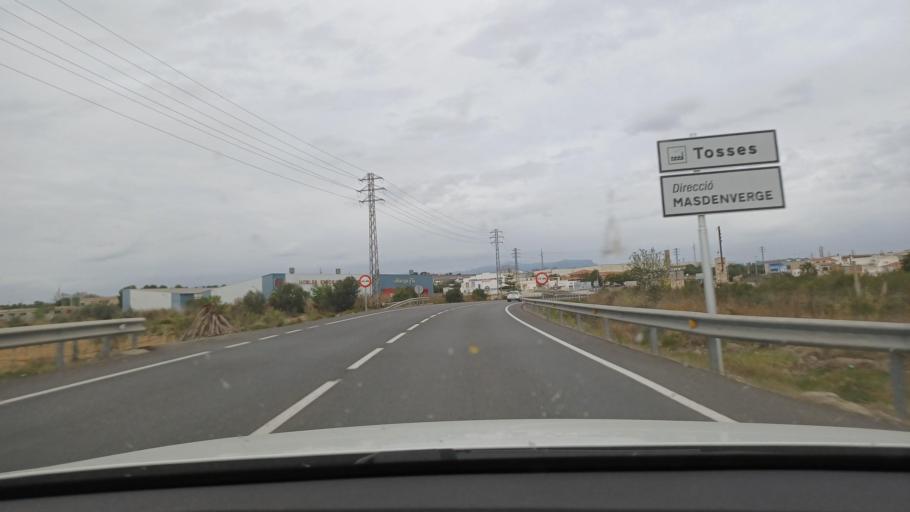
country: ES
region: Catalonia
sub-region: Provincia de Tarragona
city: Amposta
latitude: 40.6994
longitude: 0.5680
